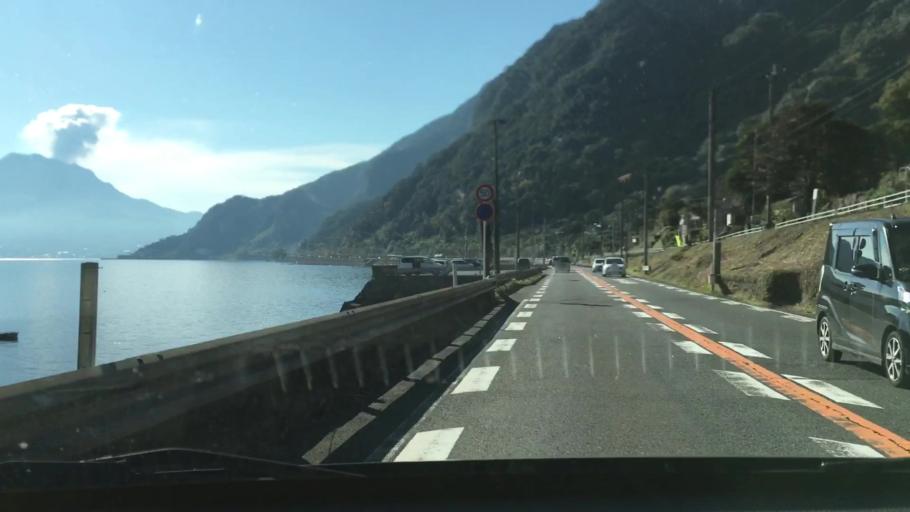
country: JP
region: Kagoshima
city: Kajiki
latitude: 31.6835
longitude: 130.6096
